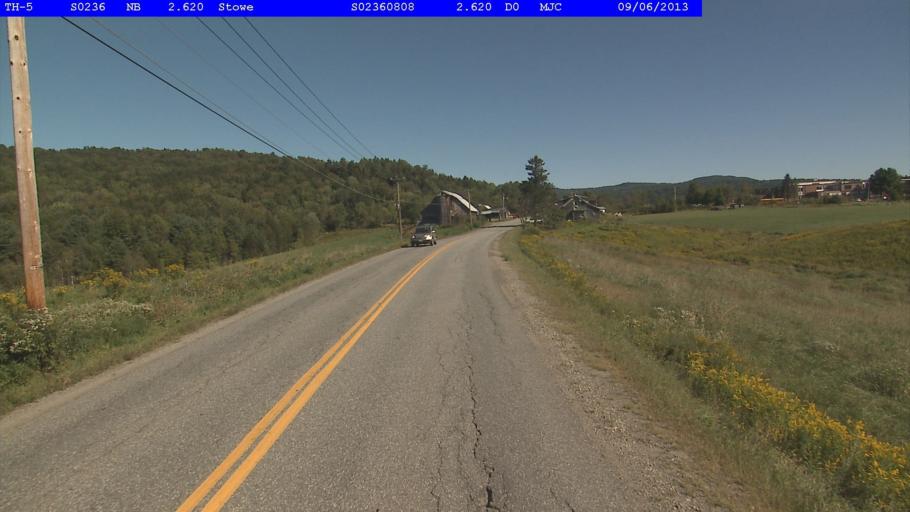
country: US
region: Vermont
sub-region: Washington County
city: Waterbury
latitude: 44.4625
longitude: -72.7290
